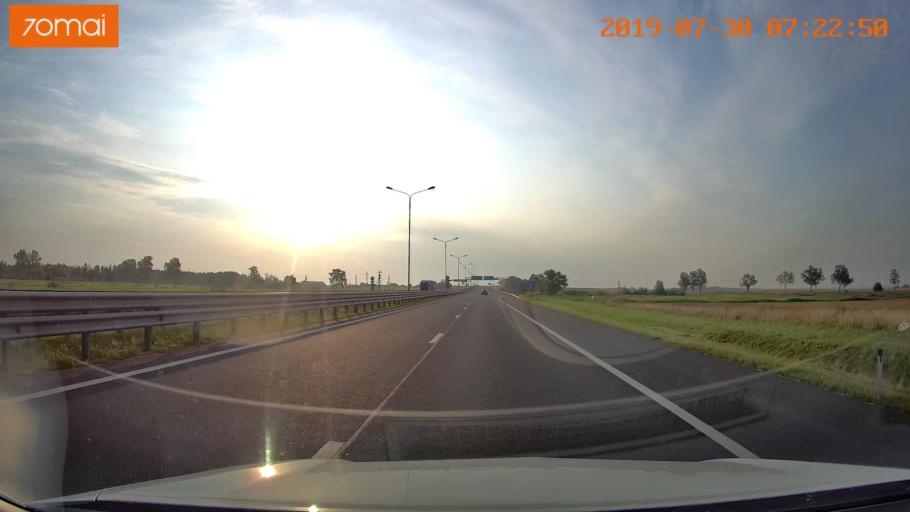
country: RU
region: Kaliningrad
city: Bol'shoe Isakovo
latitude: 54.6921
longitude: 20.7669
